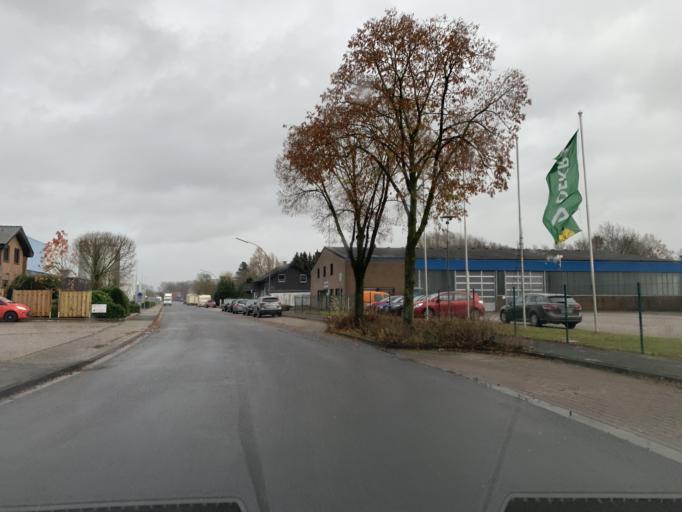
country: DE
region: North Rhine-Westphalia
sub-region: Regierungsbezirk Munster
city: Steinfurt
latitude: 52.1337
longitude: 7.4091
